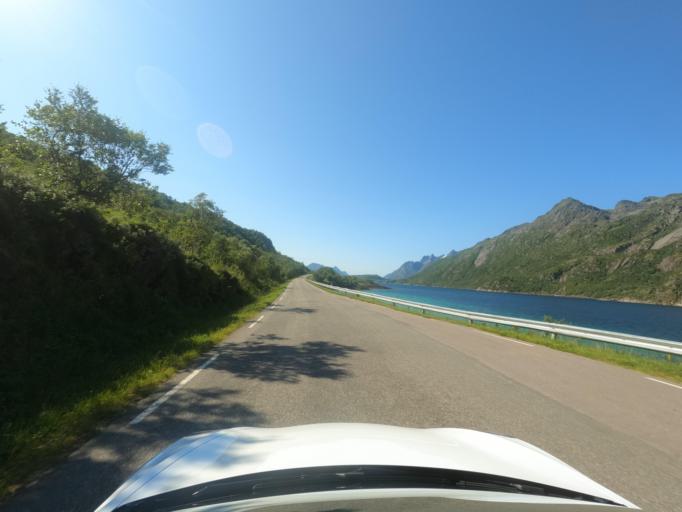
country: NO
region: Nordland
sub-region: Hadsel
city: Stokmarknes
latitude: 68.3887
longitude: 15.0977
